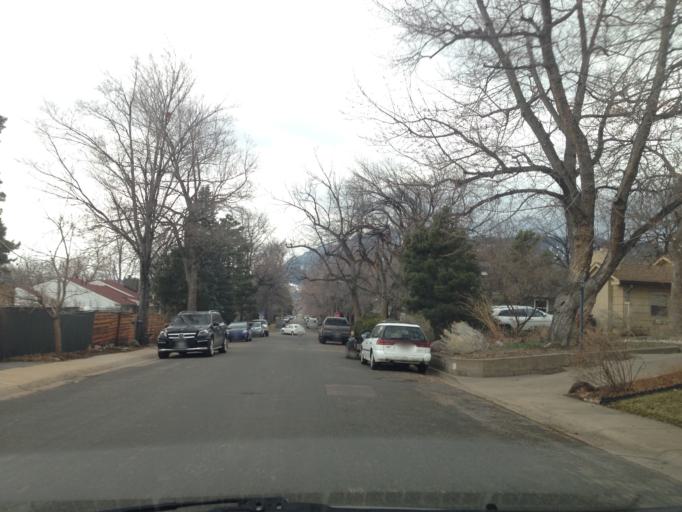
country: US
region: Colorado
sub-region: Boulder County
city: Boulder
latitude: 40.0338
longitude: -105.2904
